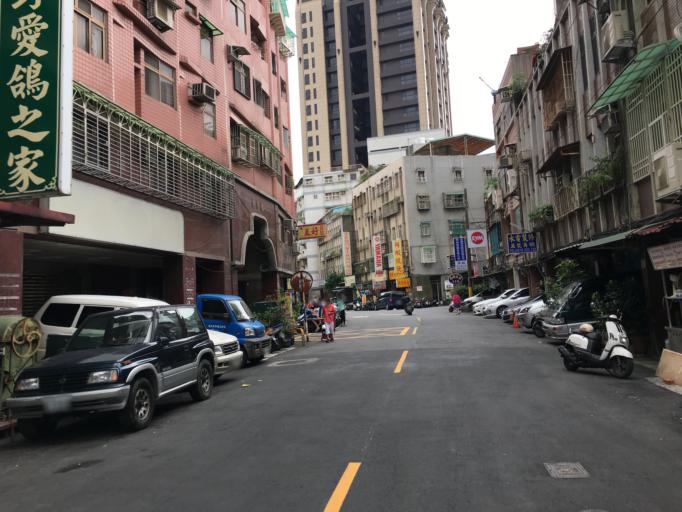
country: TW
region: Taipei
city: Taipei
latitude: 25.0653
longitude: 121.4945
